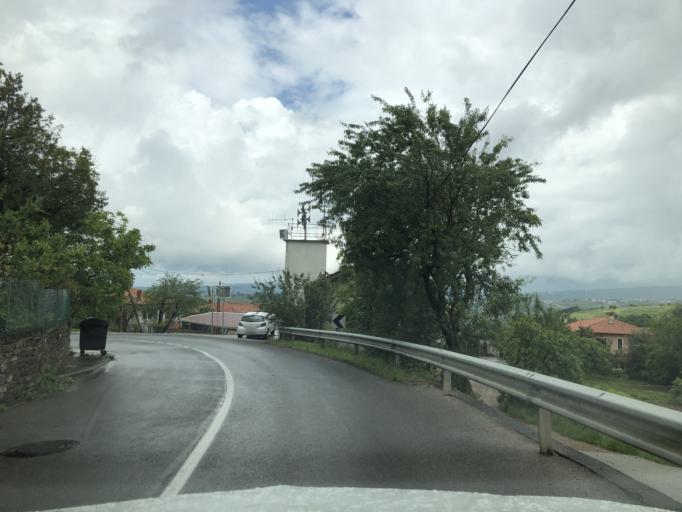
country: SI
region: Koper-Capodistria
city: Prade
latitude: 45.5032
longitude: 13.7790
